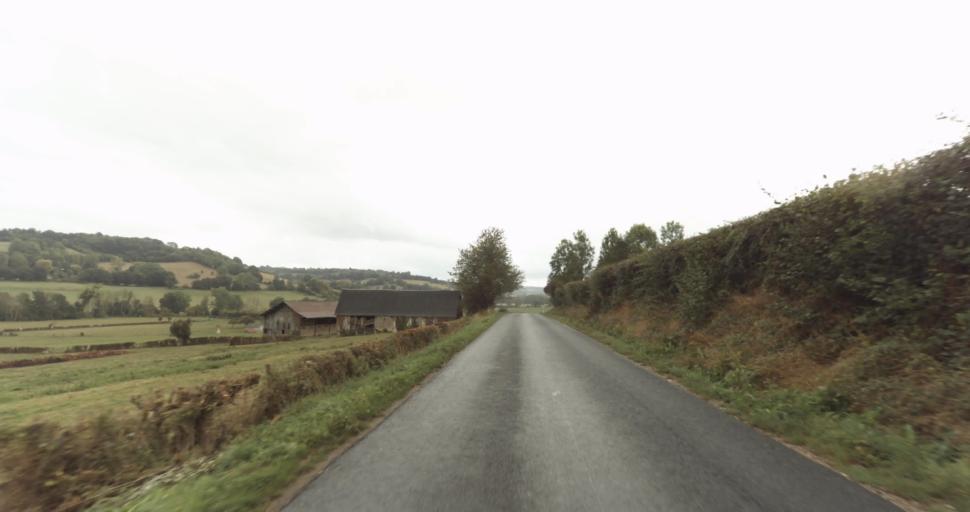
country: FR
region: Lower Normandy
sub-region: Departement de l'Orne
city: Vimoutiers
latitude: 48.8979
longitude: 0.2100
